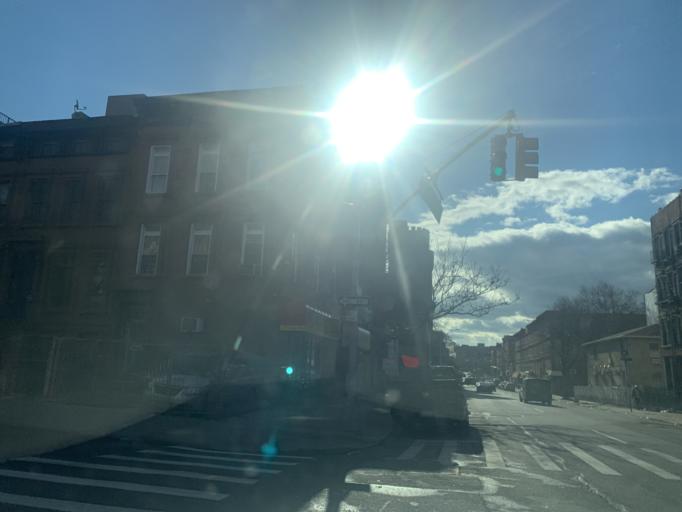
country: US
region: New York
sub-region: Kings County
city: Brooklyn
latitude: 40.6862
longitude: -73.9387
